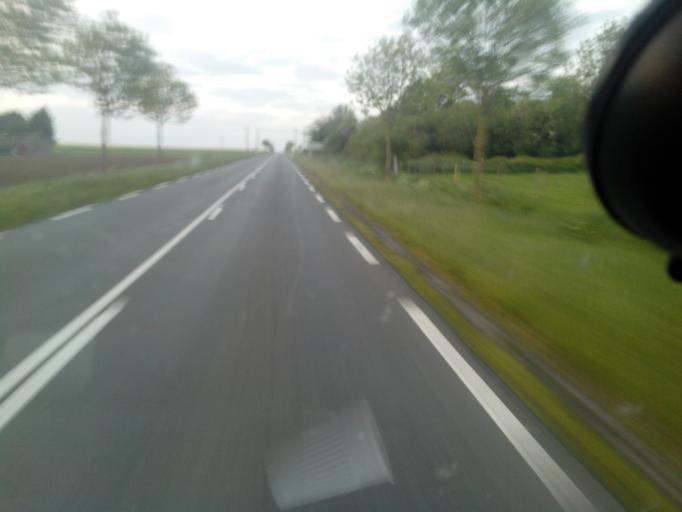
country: FR
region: Nord-Pas-de-Calais
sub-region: Departement du Pas-de-Calais
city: Hesdin
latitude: 50.3271
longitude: 2.0211
